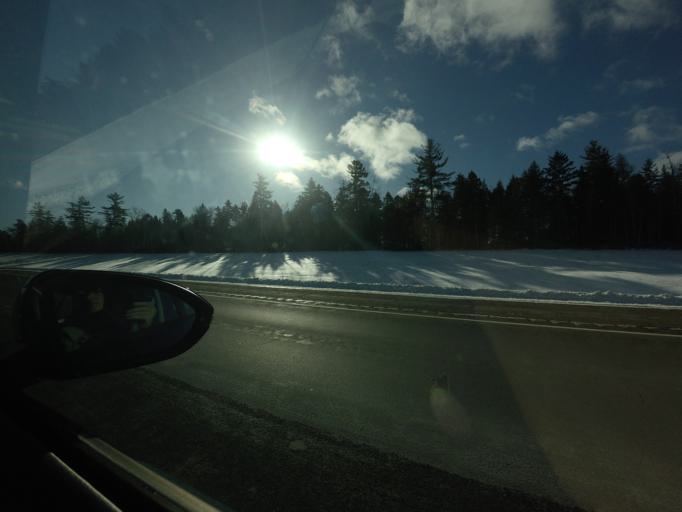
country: CA
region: New Brunswick
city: Fredericton
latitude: 45.8759
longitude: -66.6292
